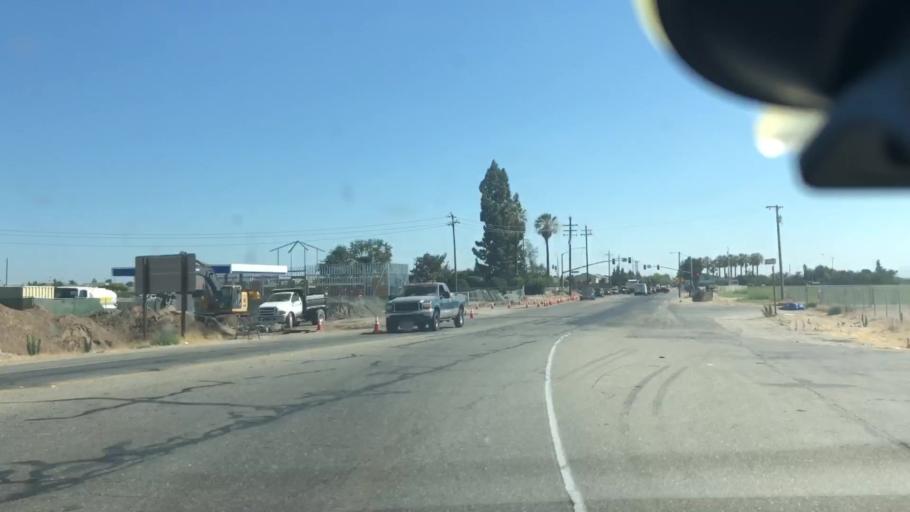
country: US
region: California
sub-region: San Joaquin County
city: Manteca
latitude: 37.7812
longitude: -121.2159
